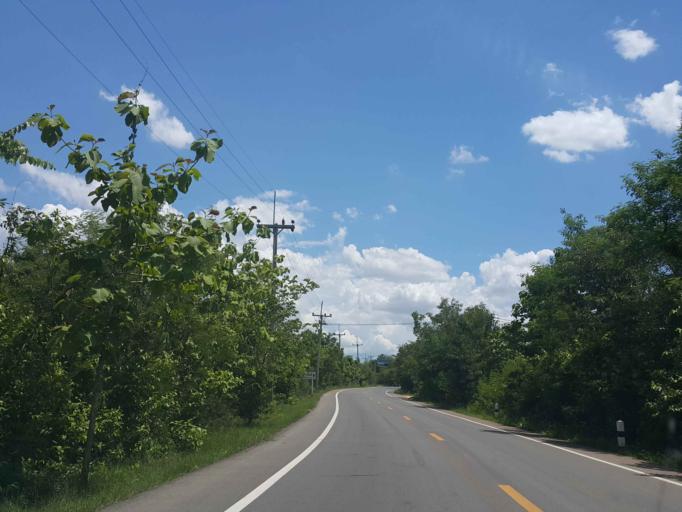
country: TH
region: Phrae
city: Nong Muang Khai
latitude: 18.1905
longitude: 100.2142
